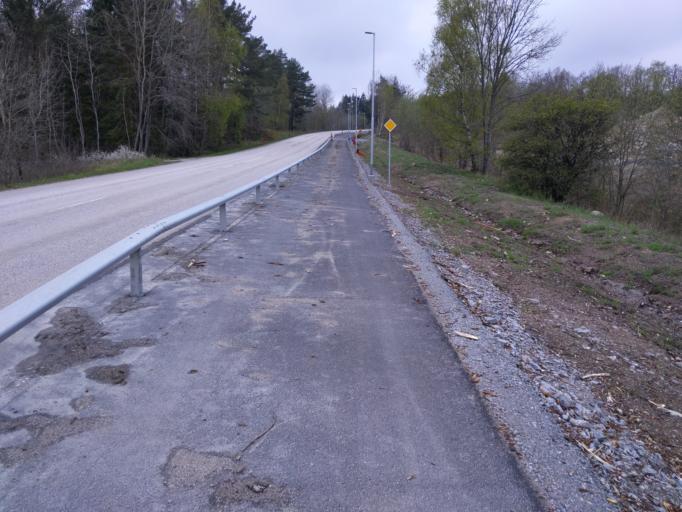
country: SE
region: Blekinge
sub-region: Karlshamns Kommun
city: Morrum
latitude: 56.1753
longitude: 14.8055
